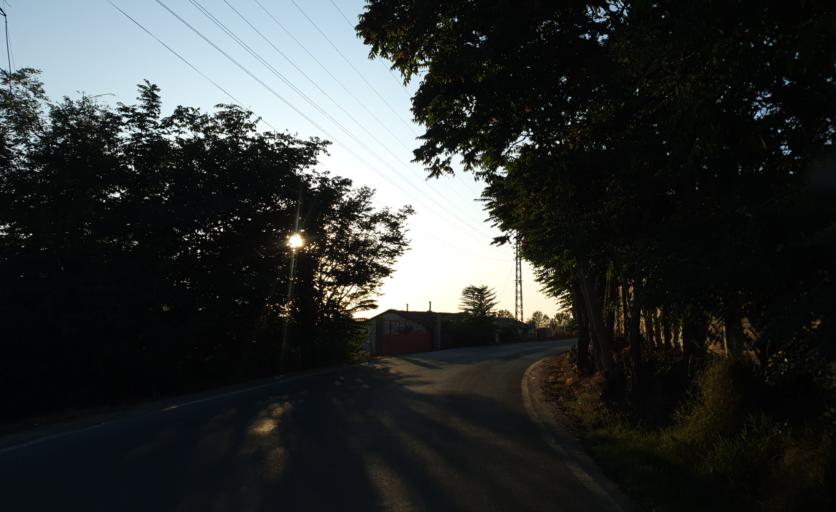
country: TR
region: Tekirdag
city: Beyazkoy
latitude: 41.3359
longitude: 27.7335
